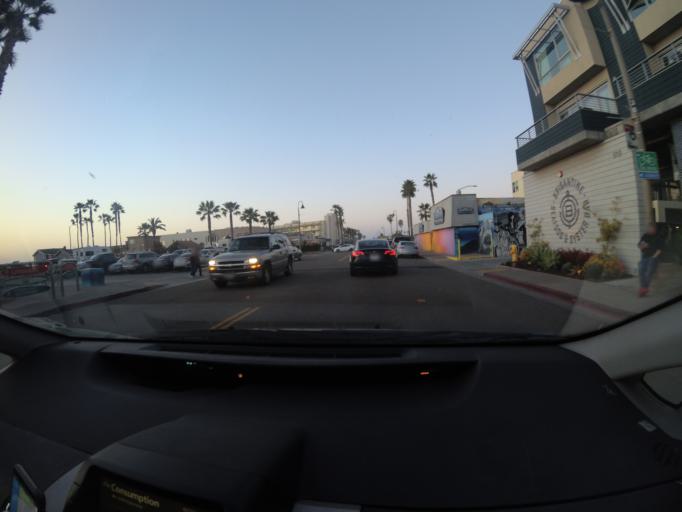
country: US
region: California
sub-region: San Diego County
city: Imperial Beach
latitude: 32.5797
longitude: -117.1316
